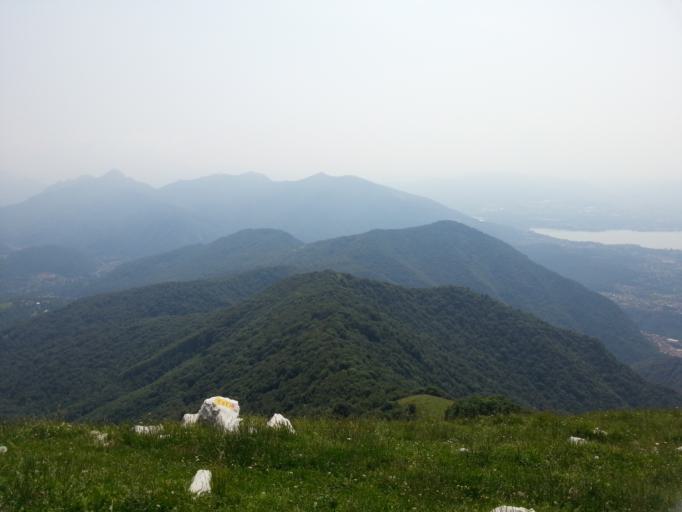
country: IT
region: Lombardy
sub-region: Provincia di Como
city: Caslino d'Erba
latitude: 45.8619
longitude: 9.2016
